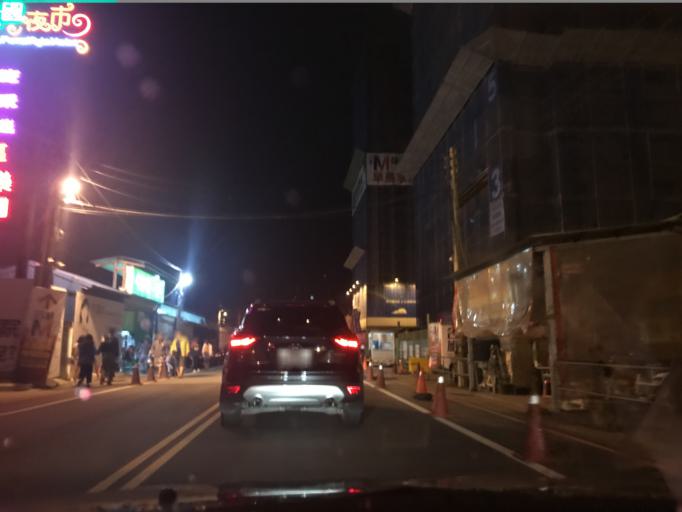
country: TW
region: Taiwan
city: Daxi
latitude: 24.9320
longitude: 121.2834
